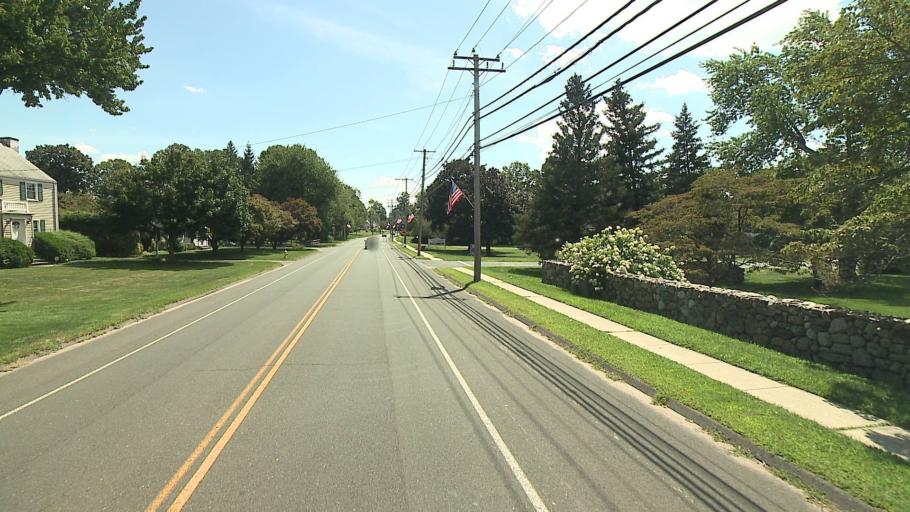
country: US
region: Connecticut
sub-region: Fairfield County
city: Trumbull
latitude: 41.2620
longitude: -73.2217
